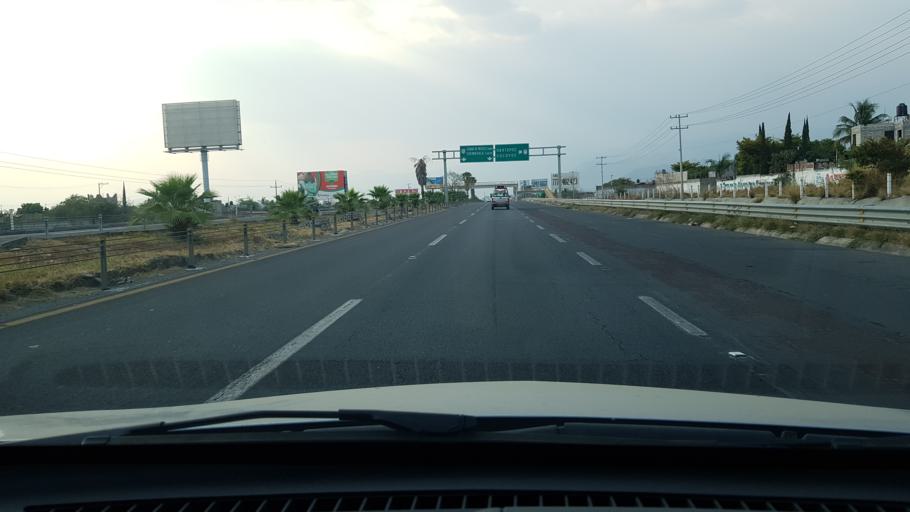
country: MX
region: Morelos
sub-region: Cuautla
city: Tierra Larga (Campo Nuevo)
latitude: 18.8544
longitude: -98.9398
